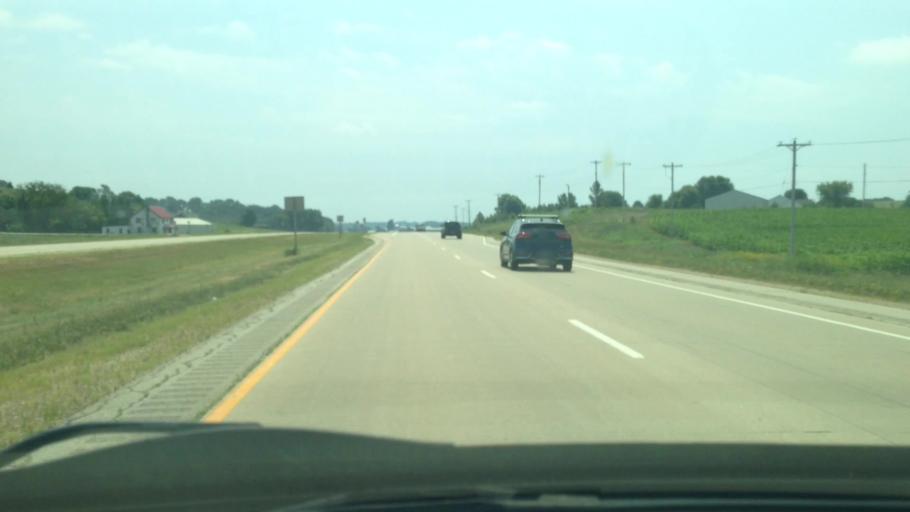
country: US
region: Wisconsin
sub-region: Dane County
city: Middleton
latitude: 43.1712
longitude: -89.5402
